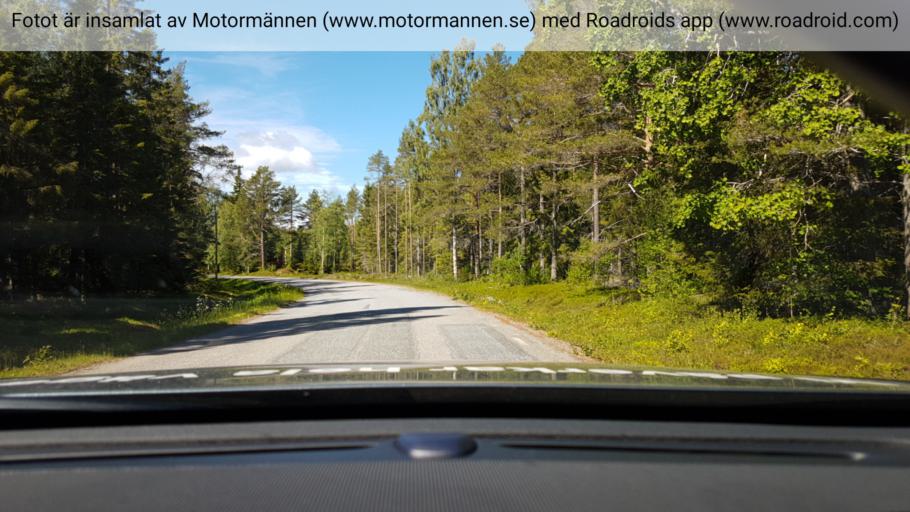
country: SE
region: Vaesterbotten
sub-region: Skelleftea Kommun
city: Burea
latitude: 64.4511
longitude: 21.5513
